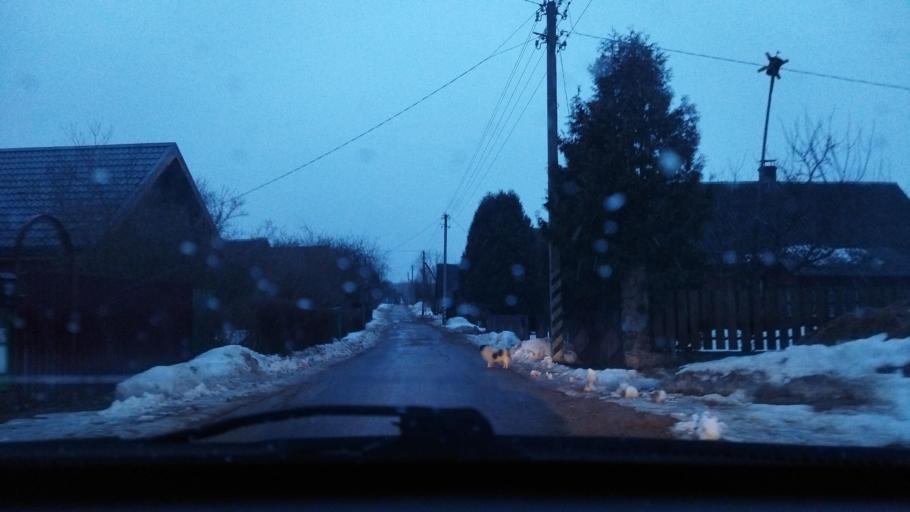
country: BY
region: Minsk
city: Svir
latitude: 54.9411
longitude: 26.4028
